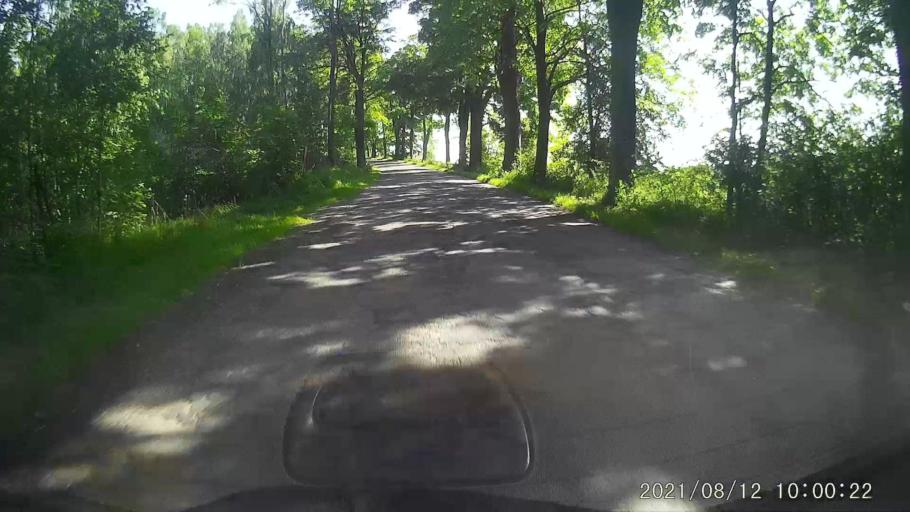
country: PL
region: Lower Silesian Voivodeship
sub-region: Powiat klodzki
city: Duszniki-Zdroj
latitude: 50.4083
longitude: 16.4093
